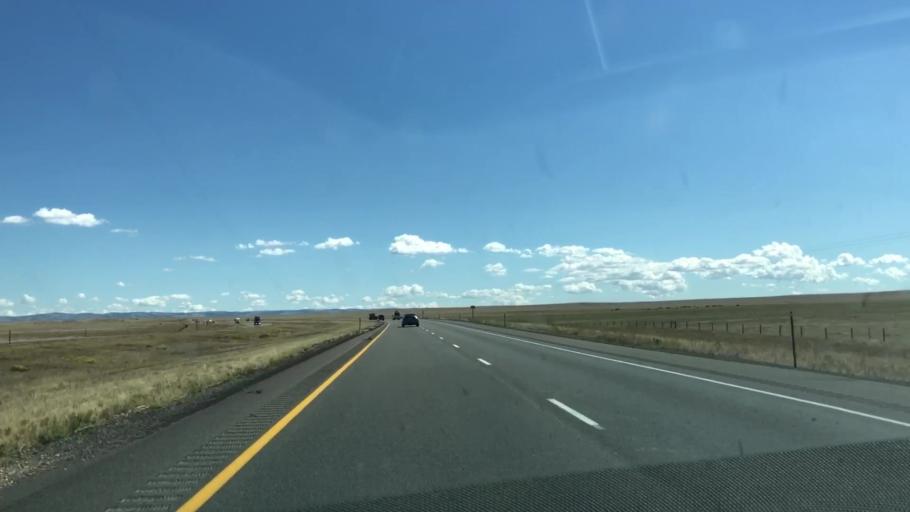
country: US
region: Wyoming
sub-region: Albany County
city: Laramie
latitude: 41.3649
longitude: -105.7797
